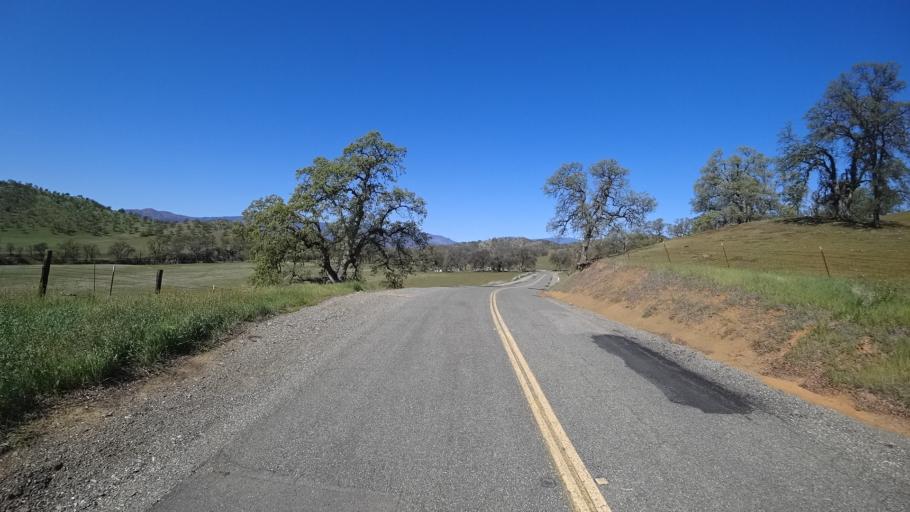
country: US
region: California
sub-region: Tehama County
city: Rancho Tehama Reserve
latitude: 39.7872
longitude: -122.4830
